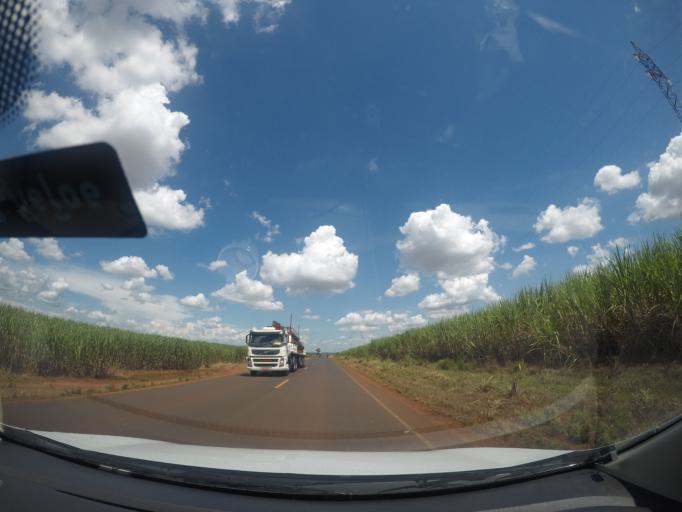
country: BR
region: Minas Gerais
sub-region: Frutal
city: Frutal
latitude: -19.8663
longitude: -48.7290
